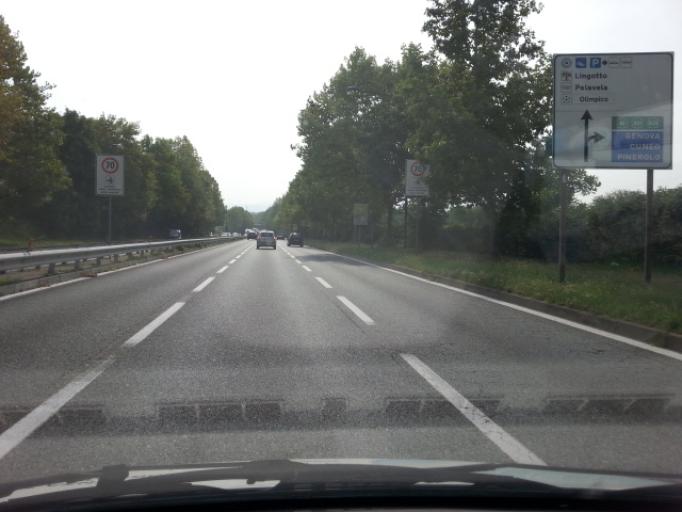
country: IT
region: Piedmont
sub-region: Provincia di Torino
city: Savonera
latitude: 45.0957
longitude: 7.6272
